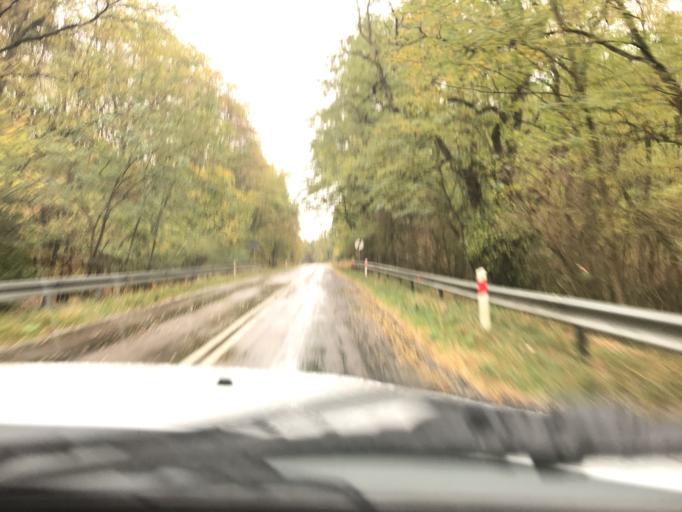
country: DE
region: Brandenburg
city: Neulewin
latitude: 52.7727
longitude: 14.3092
